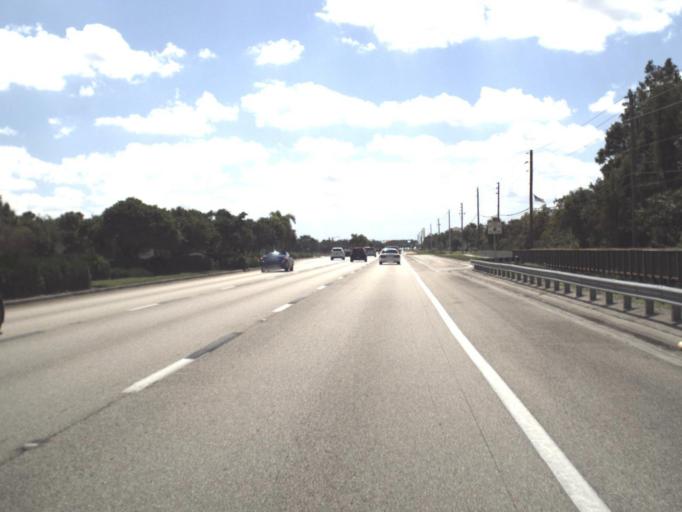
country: US
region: Florida
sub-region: Lee County
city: Estero
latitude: 26.4100
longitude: -81.8118
